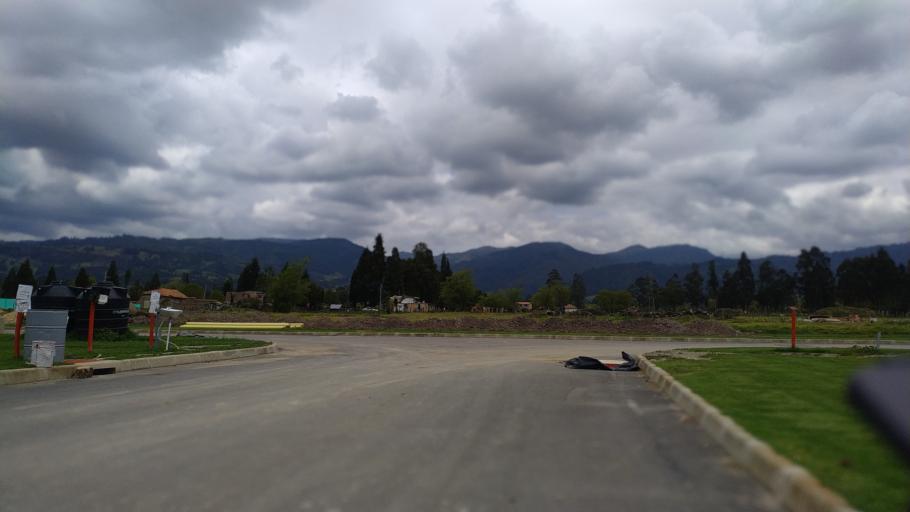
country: CO
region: Boyaca
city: Duitama
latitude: 5.7976
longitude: -73.0671
